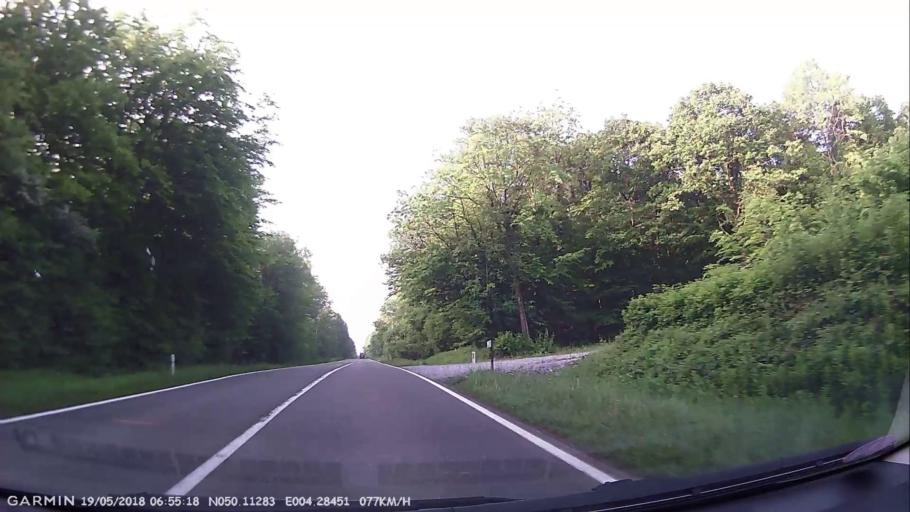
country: BE
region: Wallonia
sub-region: Province du Hainaut
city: Froidchapelle
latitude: 50.1126
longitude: 4.2846
